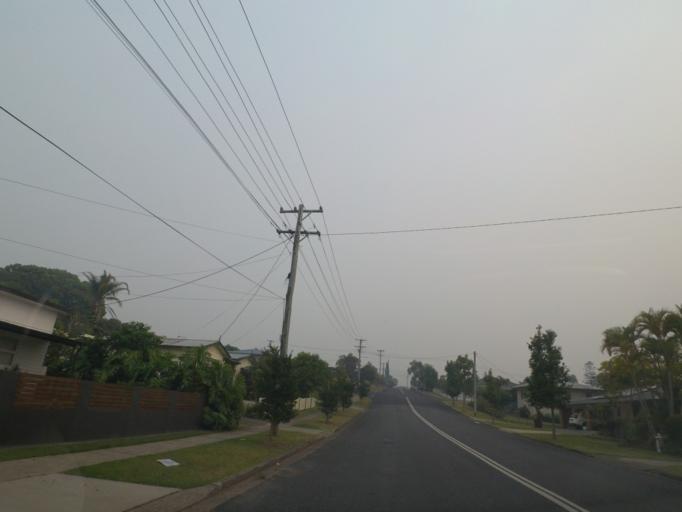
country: AU
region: New South Wales
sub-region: Coffs Harbour
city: Coffs Harbour
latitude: -30.2913
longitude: 153.1075
